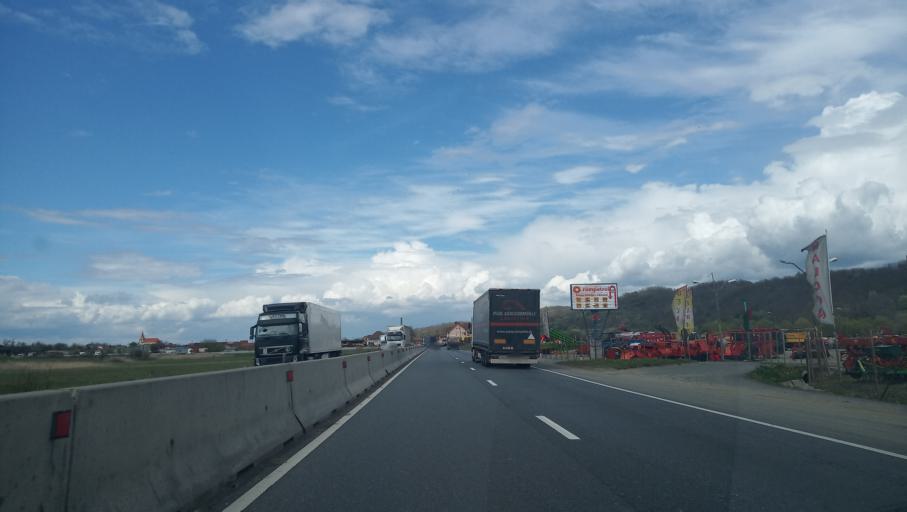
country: RO
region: Sibiu
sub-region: Comuna Selimbar
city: Vestem
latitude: 45.7083
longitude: 24.2451
